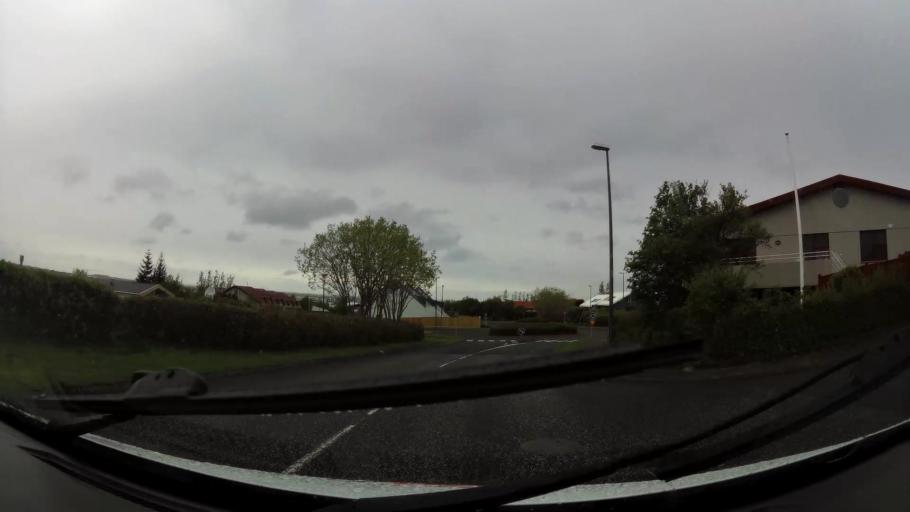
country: IS
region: Capital Region
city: Kopavogur
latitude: 64.0967
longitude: -21.8998
